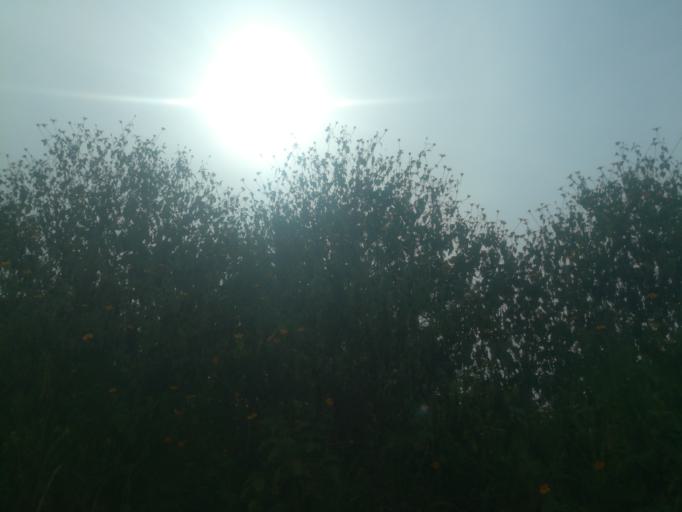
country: NG
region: Ogun
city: Ayetoro
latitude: 7.3280
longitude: 3.0672
